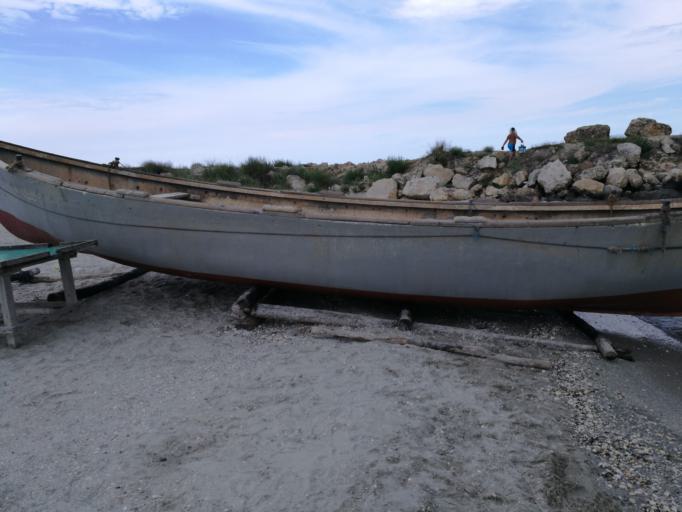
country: RO
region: Constanta
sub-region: Comuna Corbu
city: Corbu
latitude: 44.4295
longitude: 28.7687
